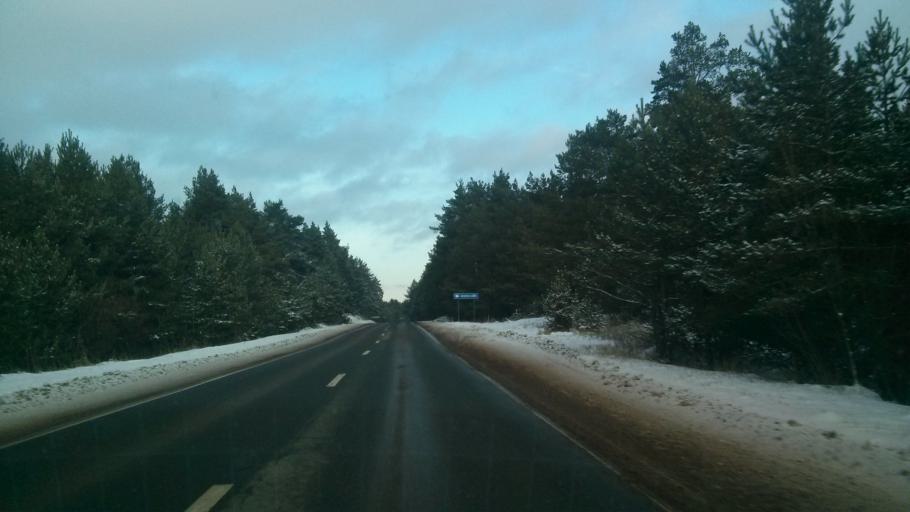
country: RU
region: Nizjnij Novgorod
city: Navashino
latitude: 55.5979
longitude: 42.1619
